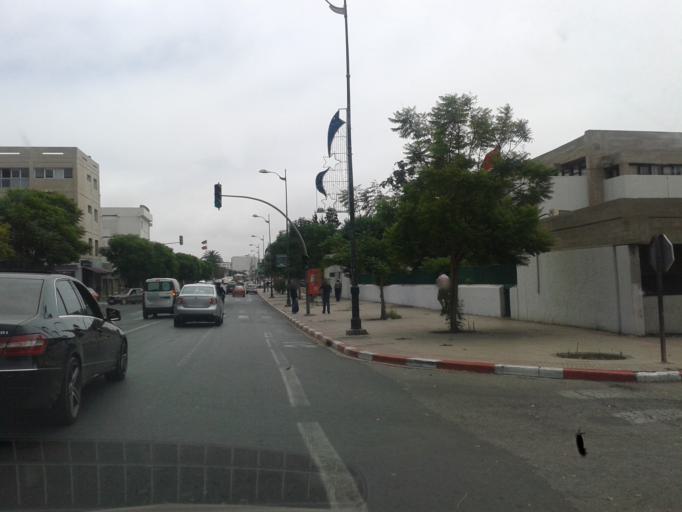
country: MA
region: Souss-Massa-Draa
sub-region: Agadir-Ida-ou-Tnan
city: Agadir
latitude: 30.4224
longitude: -9.6020
